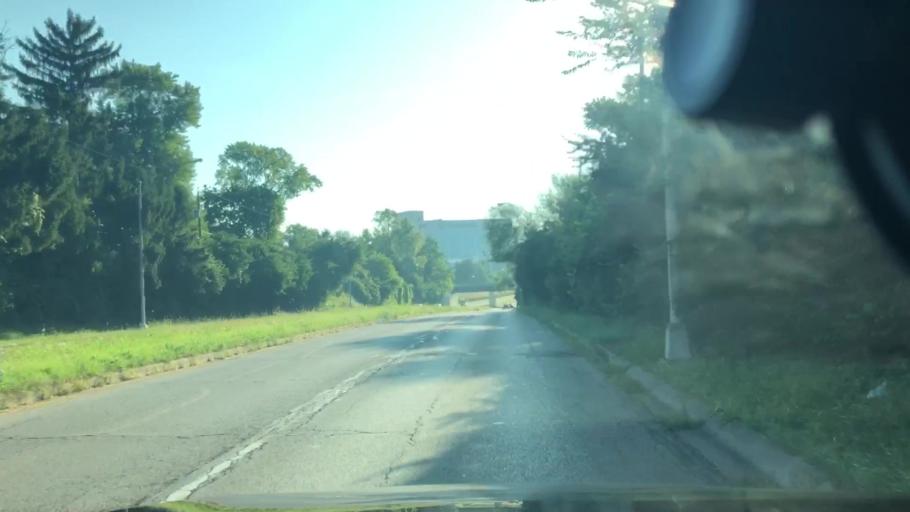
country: US
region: Ohio
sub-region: Franklin County
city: Upper Arlington
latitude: 40.0291
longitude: -83.0424
